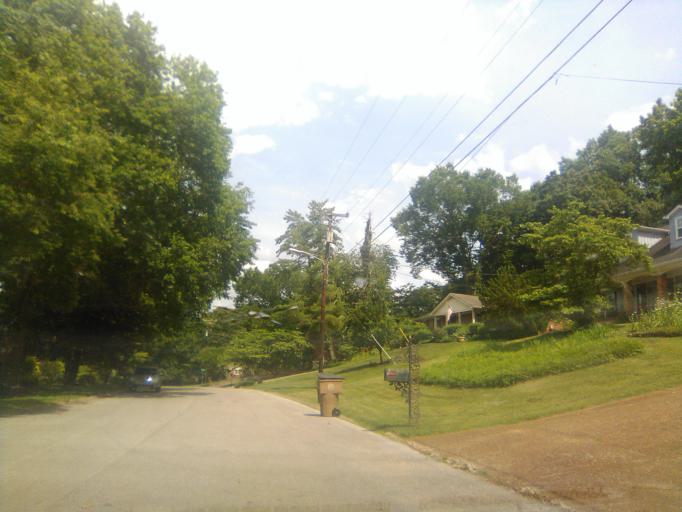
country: US
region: Tennessee
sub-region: Davidson County
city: Belle Meade
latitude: 36.0818
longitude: -86.8939
